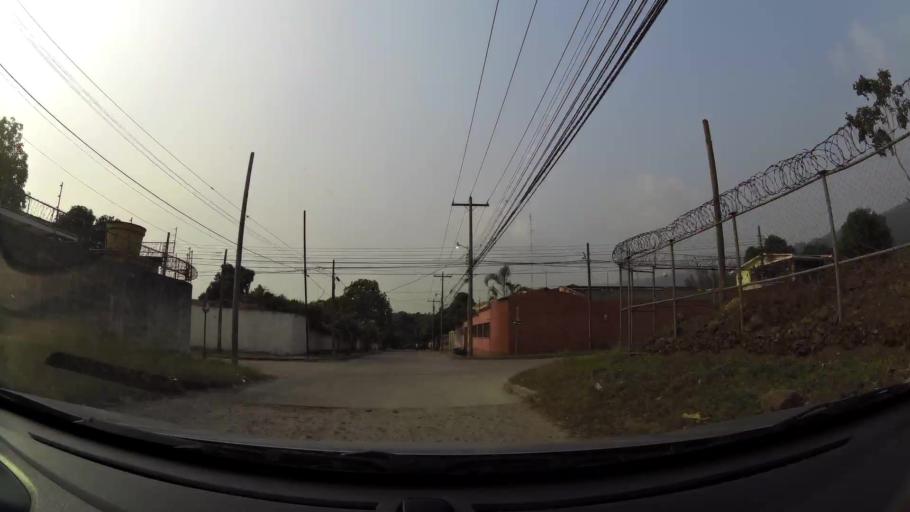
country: HN
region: Cortes
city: Armenta
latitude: 15.4848
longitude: -88.0386
